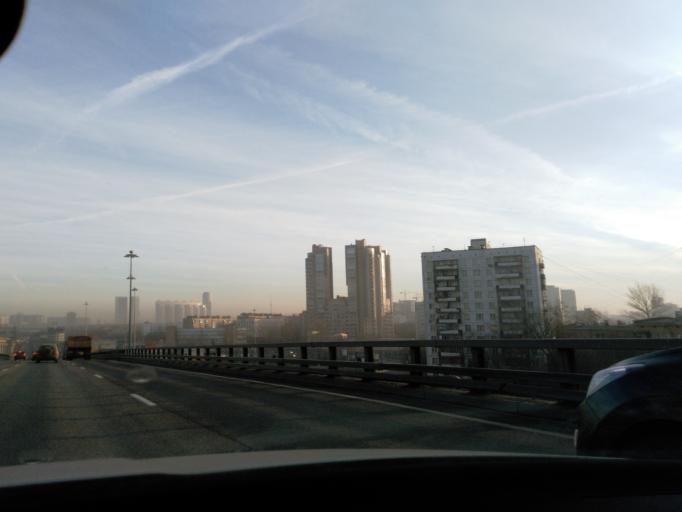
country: RU
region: Moskovskaya
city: Presnenskiy
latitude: 55.7532
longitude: 37.5321
